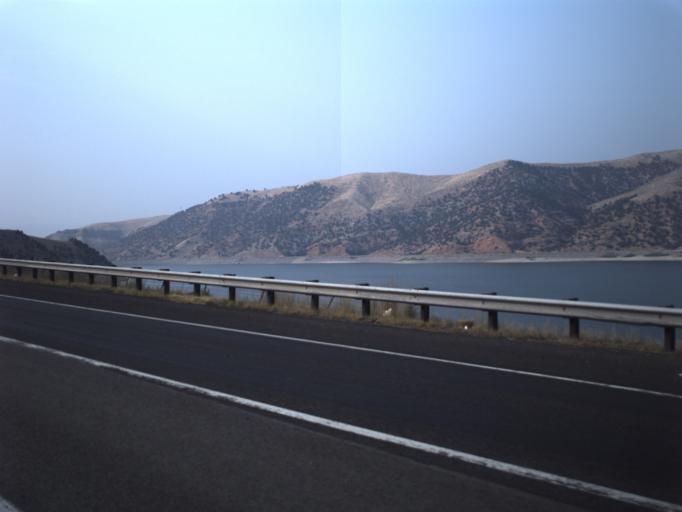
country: US
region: Utah
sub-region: Summit County
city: Coalville
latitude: 40.9473
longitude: -111.4160
